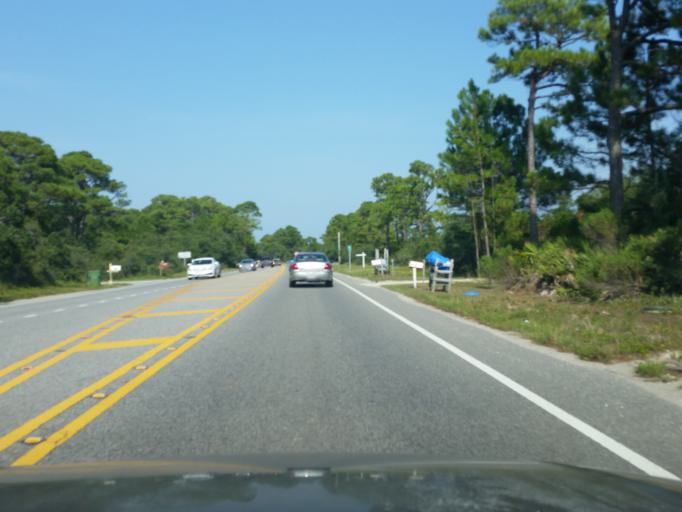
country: US
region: Alabama
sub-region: Baldwin County
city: Gulf Shores
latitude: 30.2380
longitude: -87.8754
